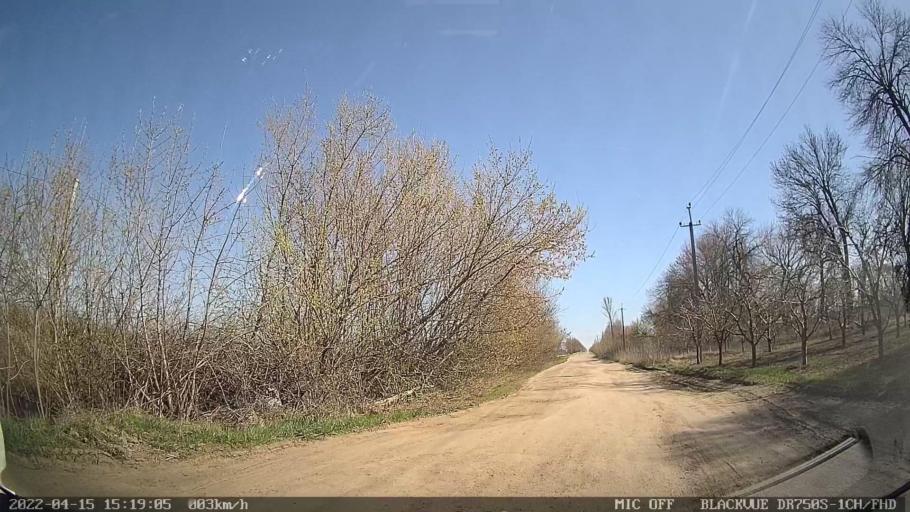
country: MD
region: Raionul Ocnita
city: Otaci
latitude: 48.3885
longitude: 27.9048
